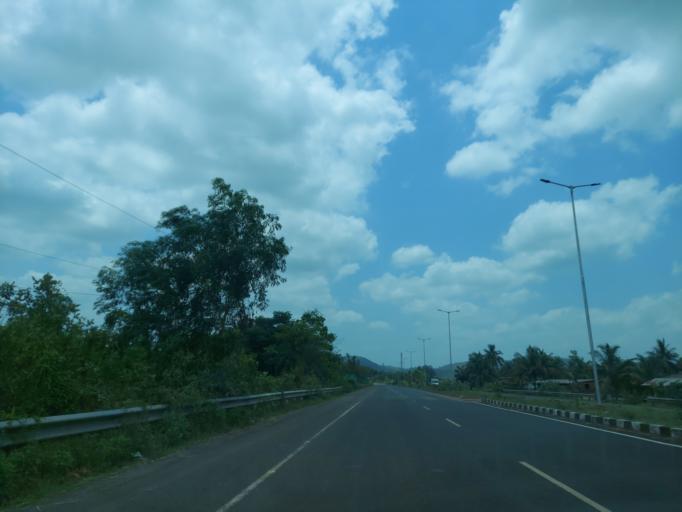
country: IN
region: Maharashtra
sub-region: Sindhudurg
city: Savantvadi
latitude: 15.8227
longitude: 73.8572
